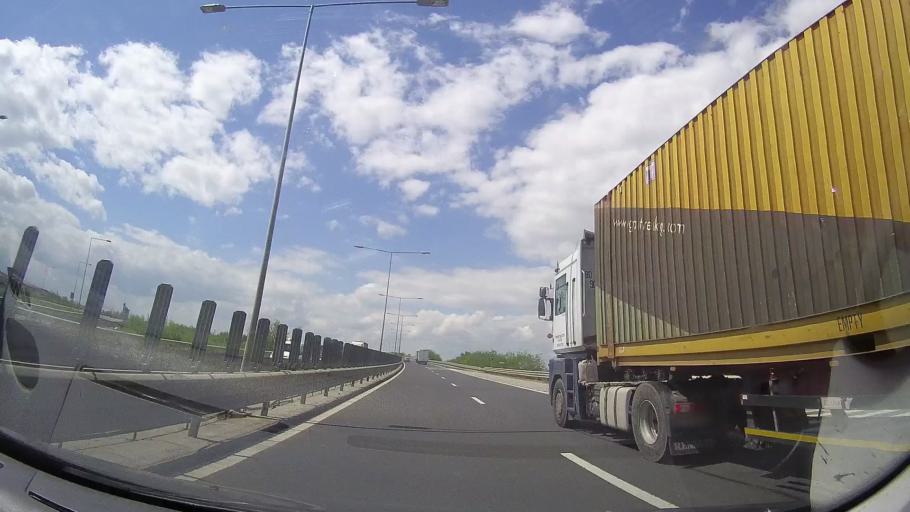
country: RO
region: Sibiu
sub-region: Comuna Selimbar
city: Selimbar
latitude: 45.7990
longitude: 24.1911
